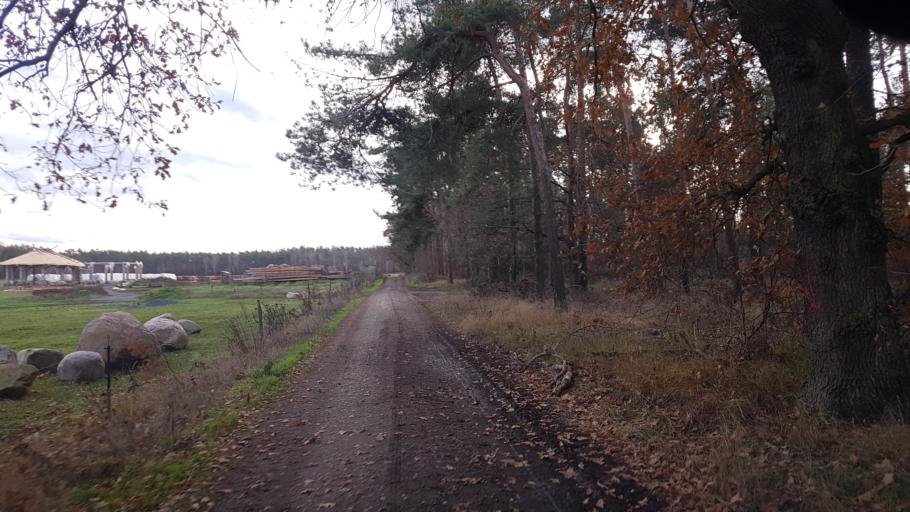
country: DE
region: Brandenburg
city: Falkenberg
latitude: 51.5728
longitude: 13.2779
